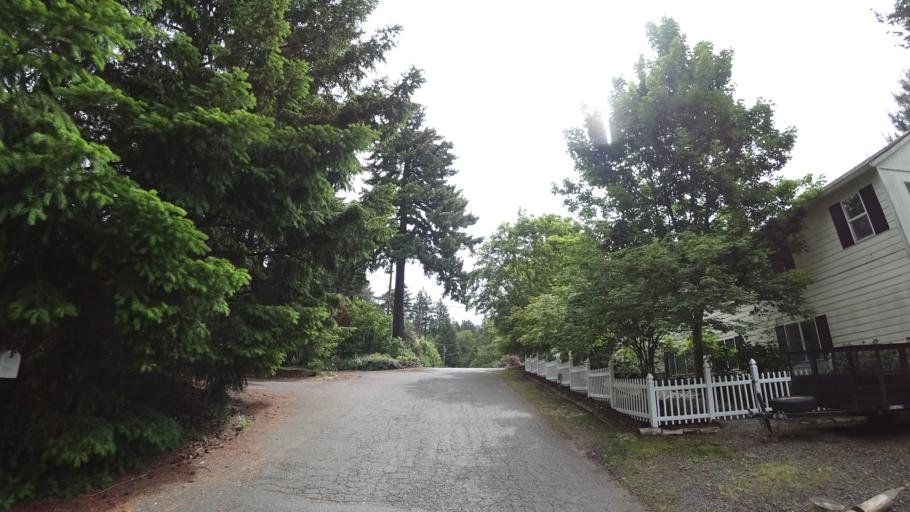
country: US
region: Oregon
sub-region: Washington County
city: Garden Home-Whitford
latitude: 45.4575
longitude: -122.7289
